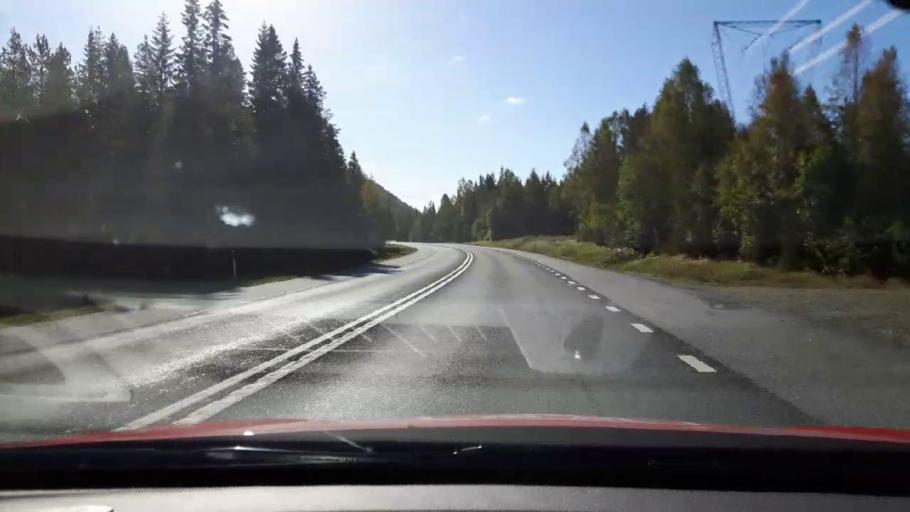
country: SE
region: Vaesternorrland
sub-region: Ange Kommun
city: Ange
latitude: 62.6657
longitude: 15.6075
